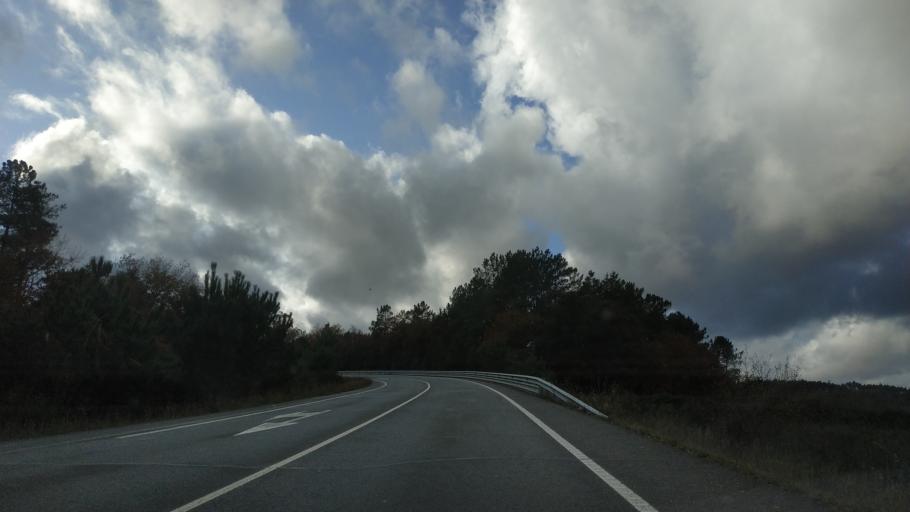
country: ES
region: Galicia
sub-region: Provincia da Coruna
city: Arzua
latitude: 42.8829
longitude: -8.1940
